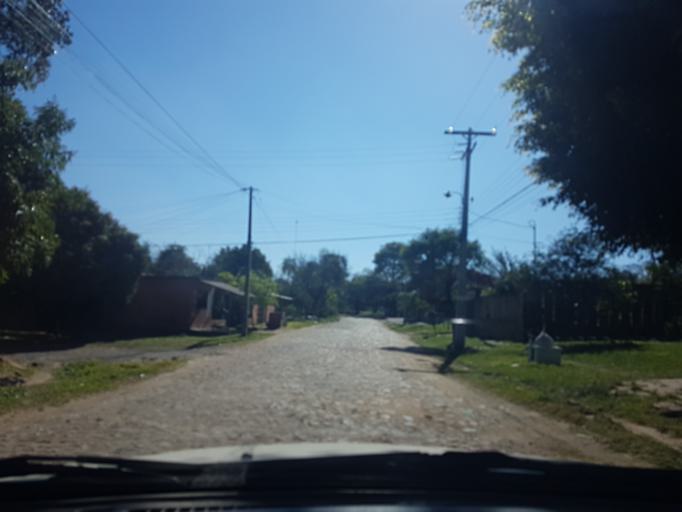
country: PY
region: Central
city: Colonia Mariano Roque Alonso
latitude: -25.2138
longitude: -57.5488
